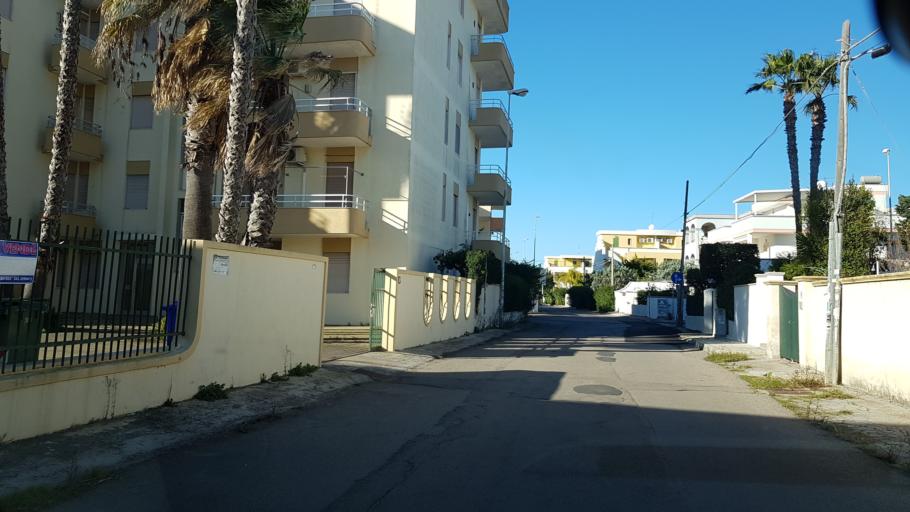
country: IT
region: Apulia
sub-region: Provincia di Lecce
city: Gallipoli
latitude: 40.0379
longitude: 18.0183
